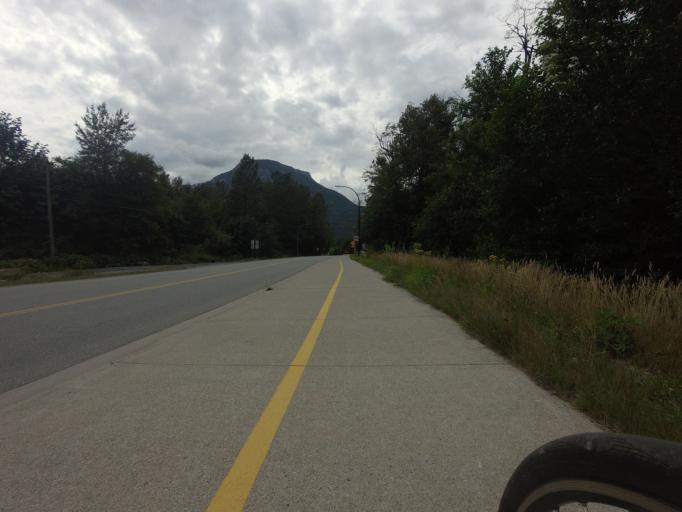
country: CA
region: British Columbia
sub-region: Greater Vancouver Regional District
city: Lions Bay
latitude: 49.7295
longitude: -123.1446
